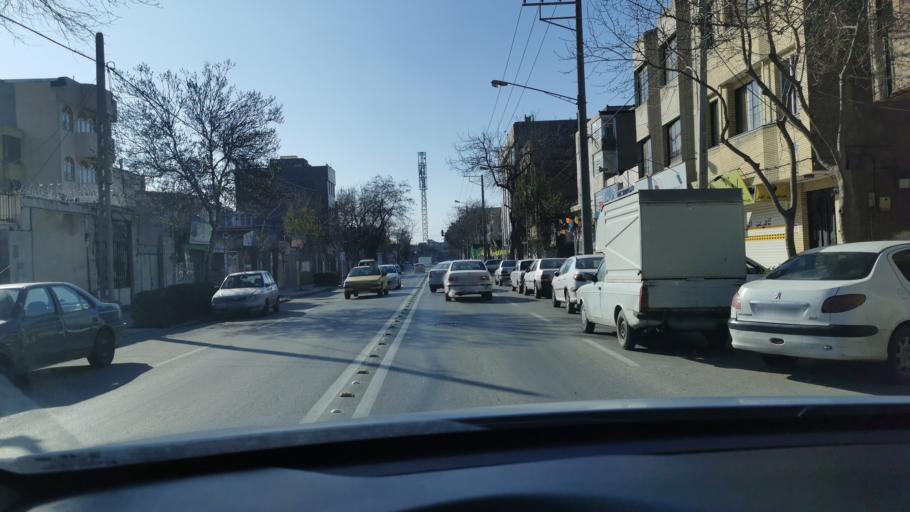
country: IR
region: Razavi Khorasan
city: Mashhad
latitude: 36.2776
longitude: 59.5751
